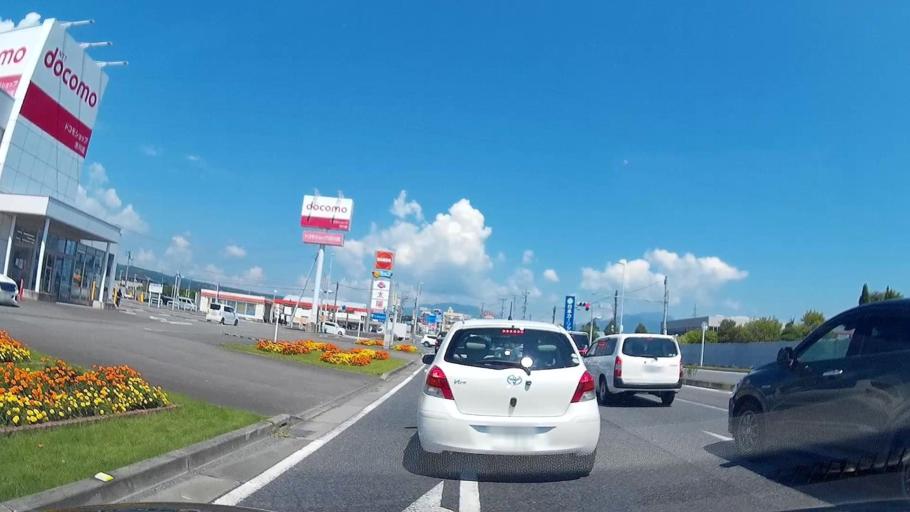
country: JP
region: Gunma
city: Shibukawa
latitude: 36.4739
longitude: 139.0229
